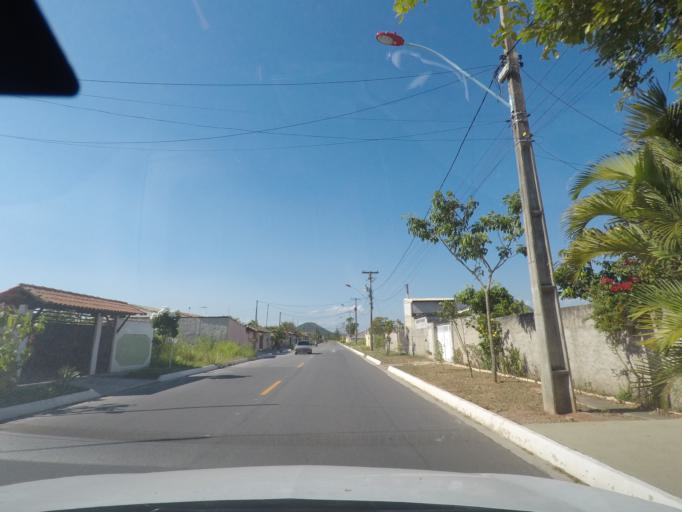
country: BR
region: Rio de Janeiro
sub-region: Marica
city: Marica
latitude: -22.9609
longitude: -42.9271
